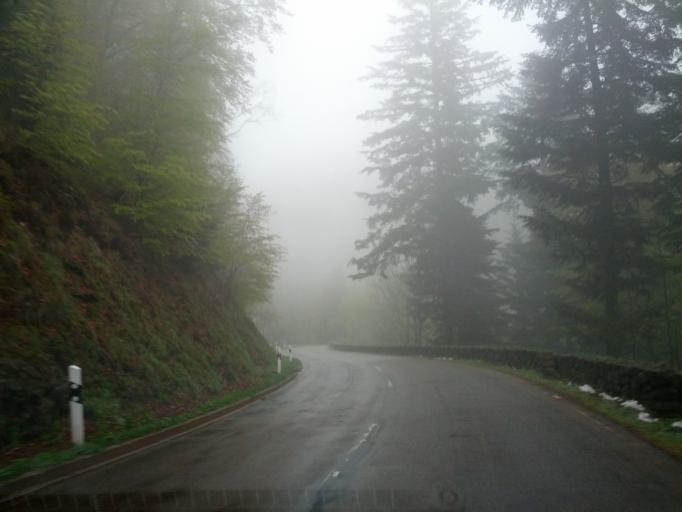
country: DE
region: Baden-Wuerttemberg
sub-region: Freiburg Region
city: Wieden
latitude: 47.8653
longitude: 7.8532
